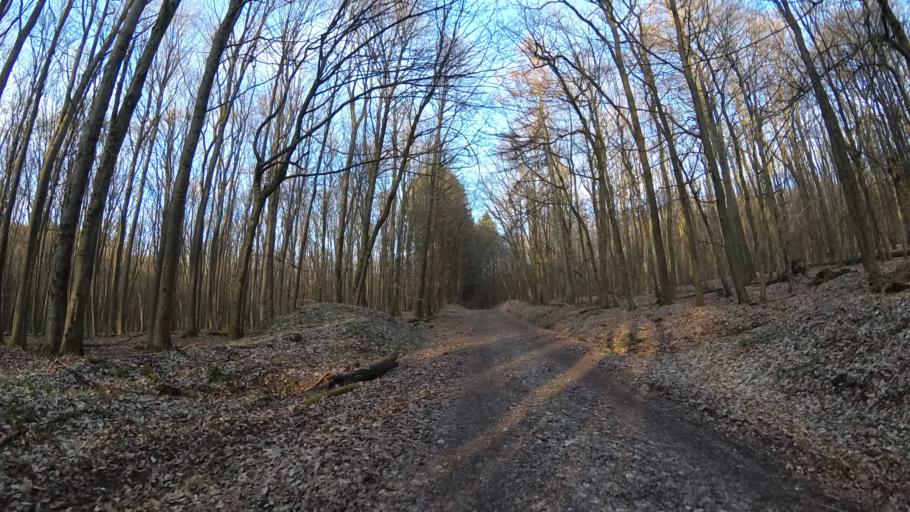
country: DE
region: Saarland
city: Marpingen
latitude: 49.4237
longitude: 7.0428
